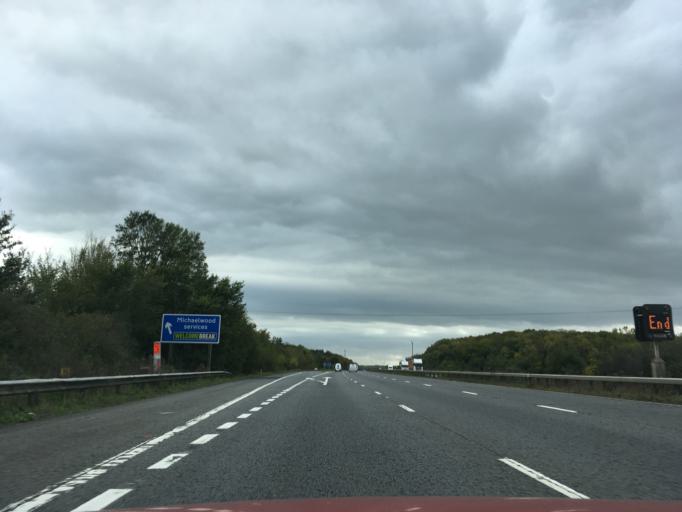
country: GB
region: England
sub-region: South Gloucestershire
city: Charfield
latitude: 51.6616
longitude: -2.4187
